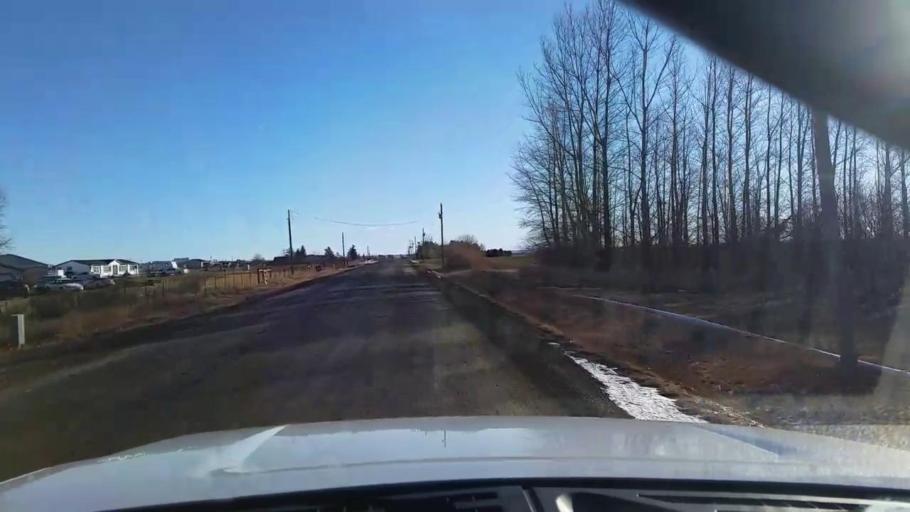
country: US
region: Colorado
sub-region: Larimer County
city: Wellington
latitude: 40.7696
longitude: -105.0834
